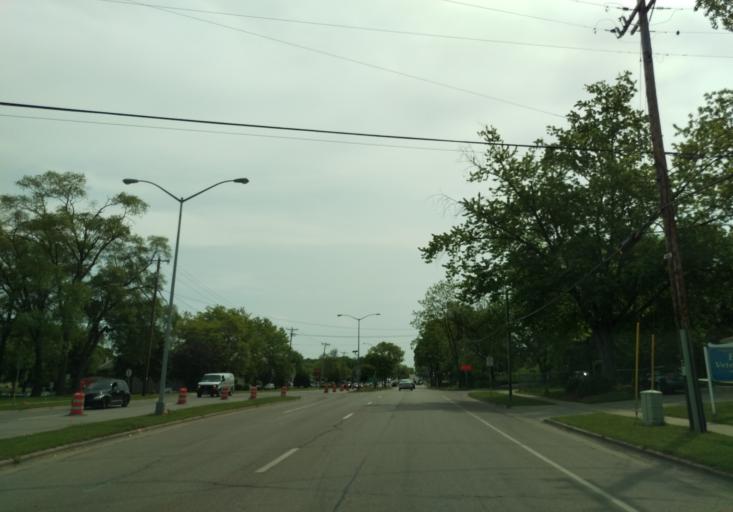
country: US
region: Wisconsin
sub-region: Dane County
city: Monona
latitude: 43.0841
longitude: -89.3064
